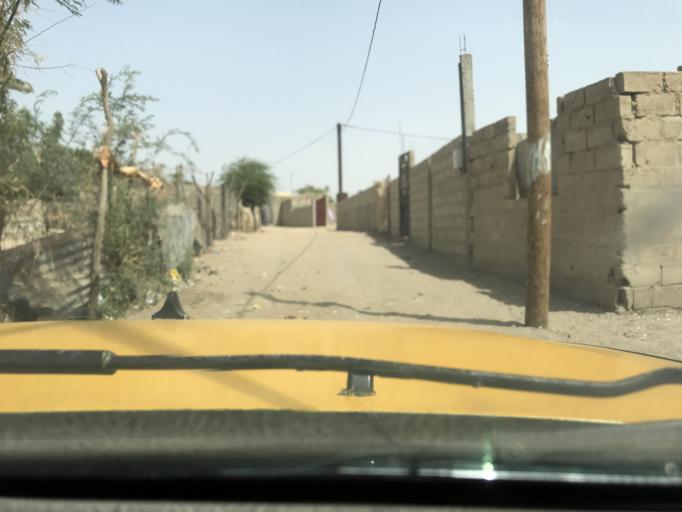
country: SN
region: Saint-Louis
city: Saint-Louis
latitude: 16.0177
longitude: -16.4465
